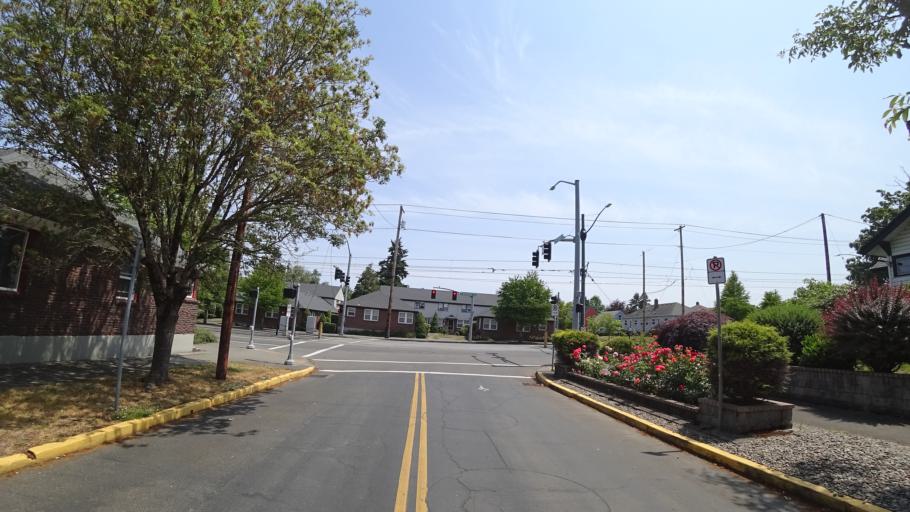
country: US
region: Oregon
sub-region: Multnomah County
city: Portland
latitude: 45.5796
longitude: -122.6824
